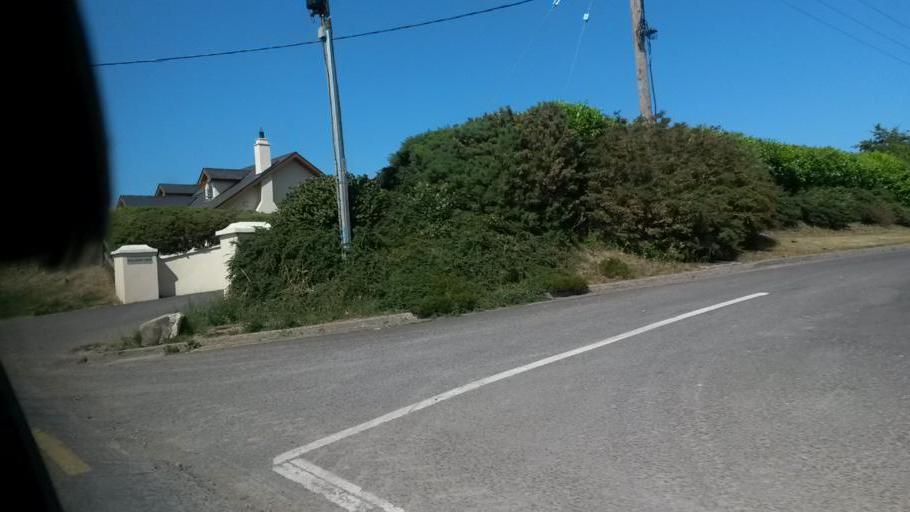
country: IE
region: Leinster
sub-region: An Mhi
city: Stamullin
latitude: 53.5367
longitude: -6.2707
